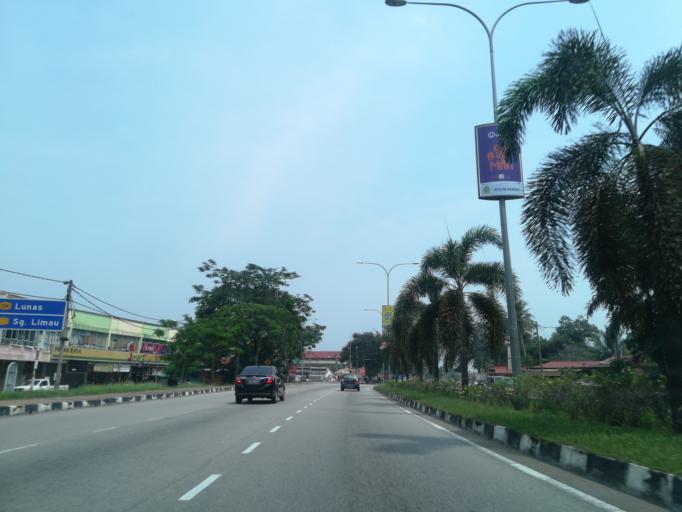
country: MY
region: Kedah
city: Kulim
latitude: 5.4132
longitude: 100.5426
